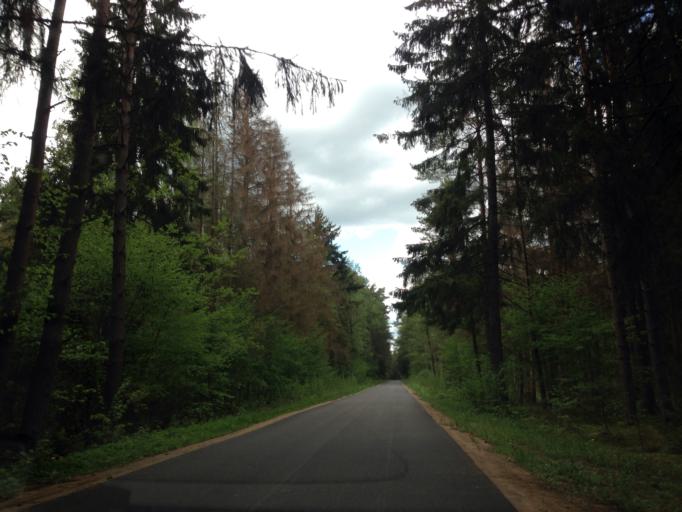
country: PL
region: Podlasie
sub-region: Powiat moniecki
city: Goniadz
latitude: 53.3553
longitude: 22.5988
